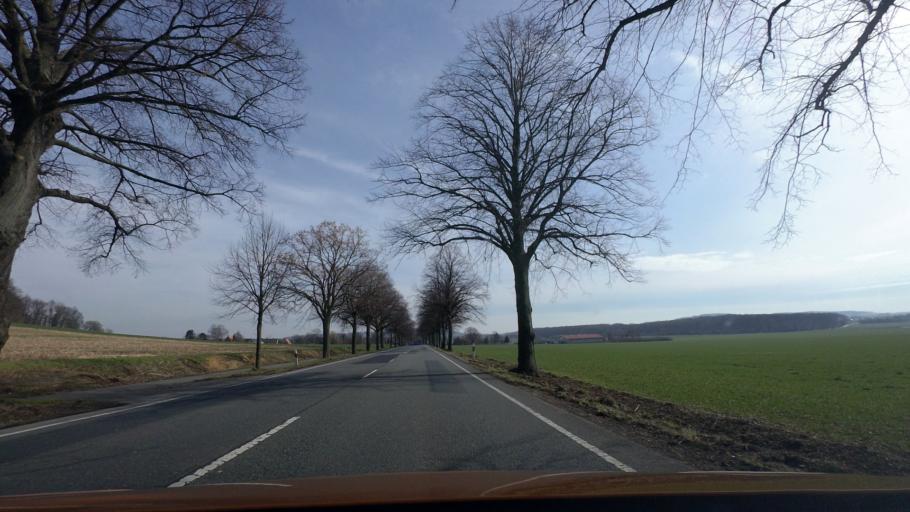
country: DE
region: Lower Saxony
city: Grossgoltern
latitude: 52.3401
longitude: 9.5377
